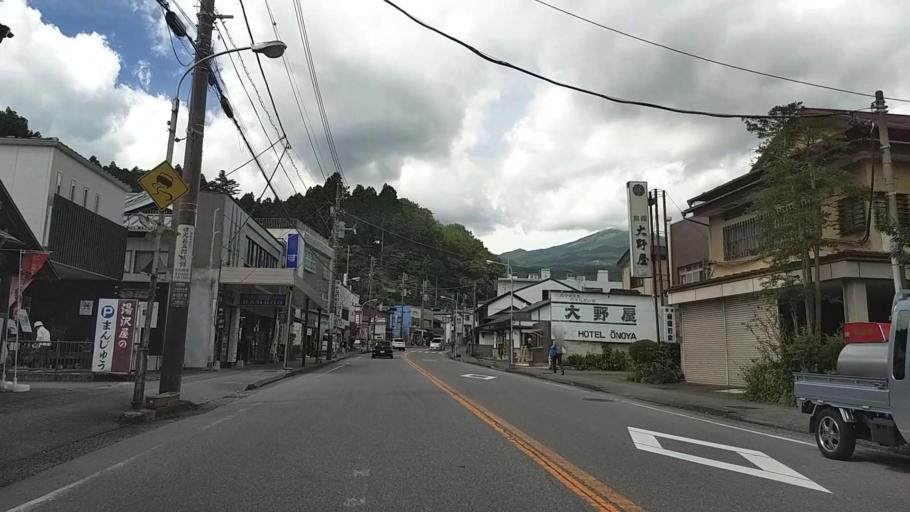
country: JP
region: Tochigi
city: Nikko
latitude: 36.7508
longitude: 139.6092
